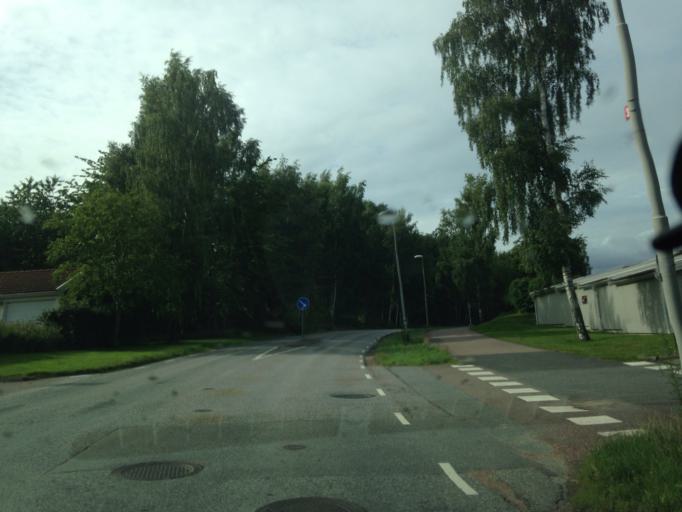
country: SE
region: Vaestra Goetaland
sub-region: Goteborg
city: Goeteborg
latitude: 57.7588
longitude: 11.9660
